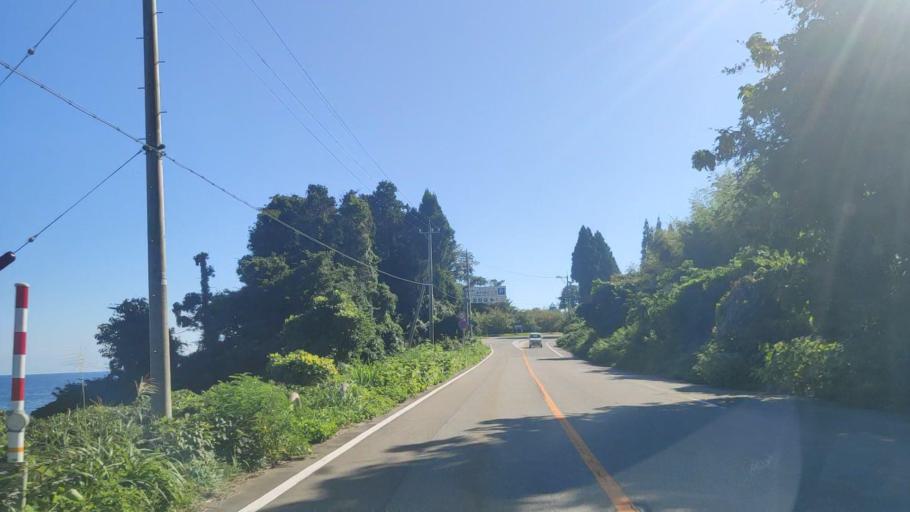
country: JP
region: Ishikawa
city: Nanao
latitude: 37.2691
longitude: 137.0948
